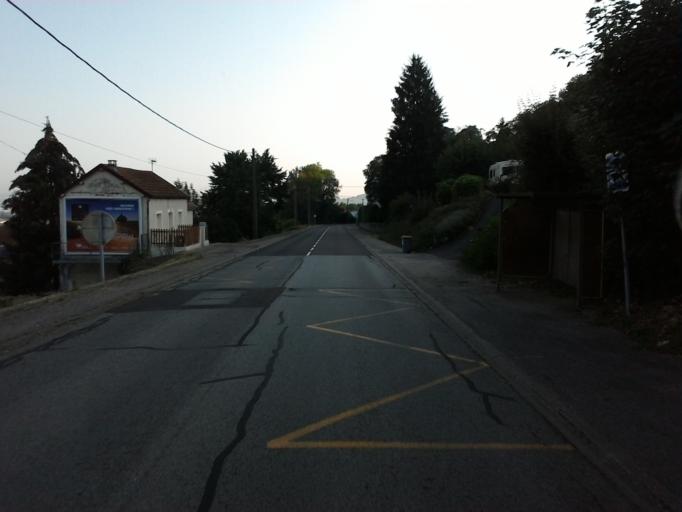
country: FR
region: Franche-Comte
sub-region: Departement de la Haute-Saone
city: Echenoz-la-Meline
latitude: 47.5946
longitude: 6.1389
